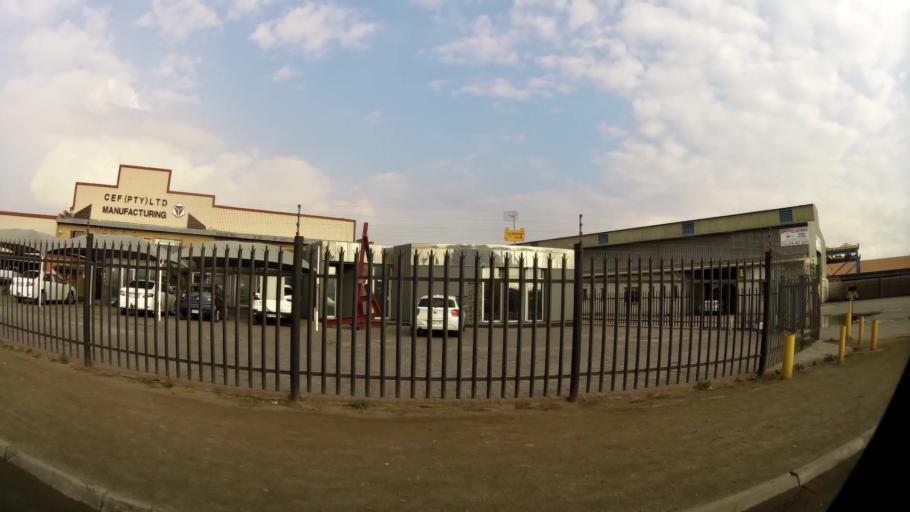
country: ZA
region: Gauteng
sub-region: Sedibeng District Municipality
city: Vereeniging
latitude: -26.6842
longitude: 27.9106
